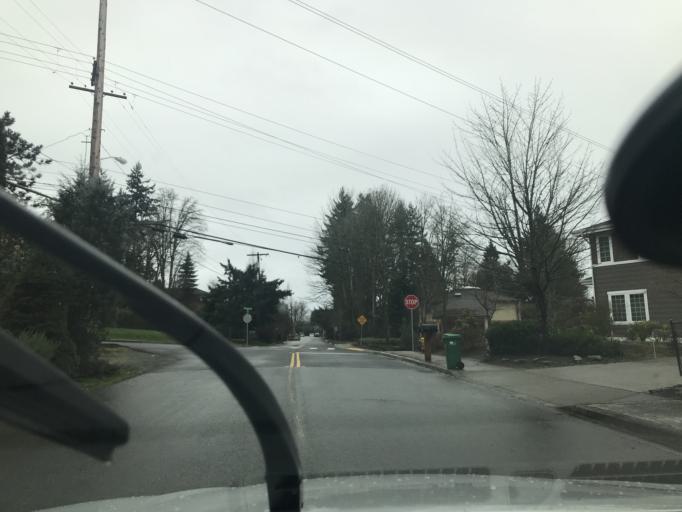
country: US
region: Washington
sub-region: King County
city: Kirkland
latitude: 47.6759
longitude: -122.1872
